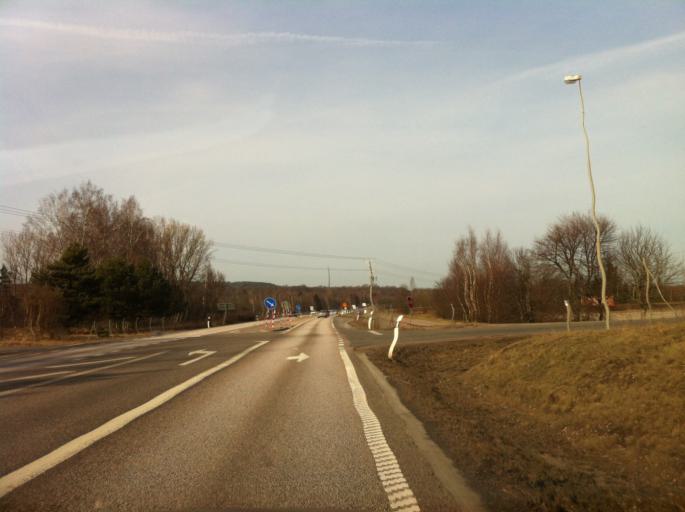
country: SE
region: Vaestra Goetaland
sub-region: Skovde Kommun
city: Stopen
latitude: 58.4429
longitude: 13.8539
